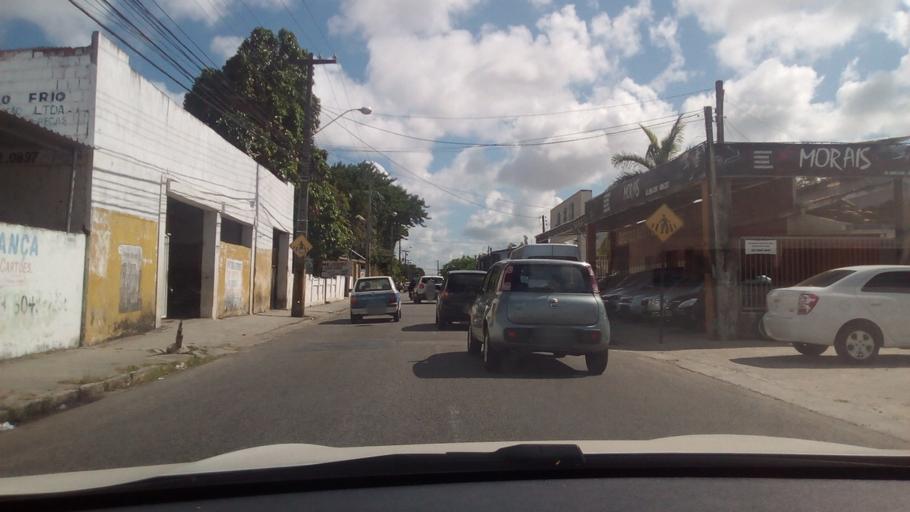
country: BR
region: Paraiba
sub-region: Joao Pessoa
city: Joao Pessoa
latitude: -7.1273
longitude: -34.8714
